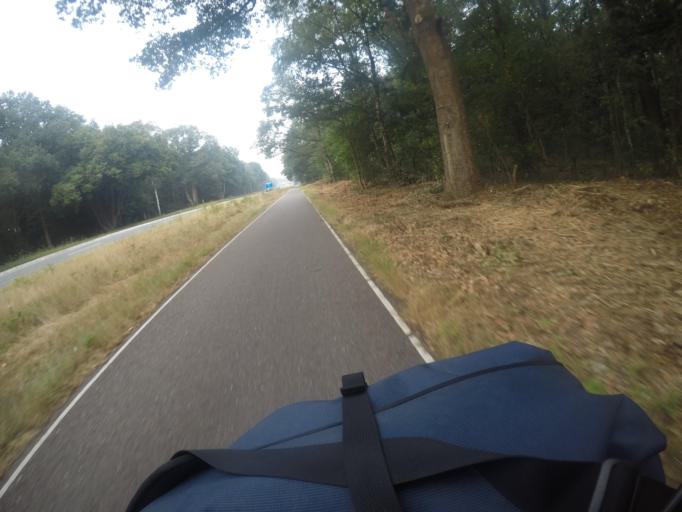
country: NL
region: Gelderland
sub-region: Gemeente Renkum
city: Oosterbeek
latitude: 52.0129
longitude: 5.8260
